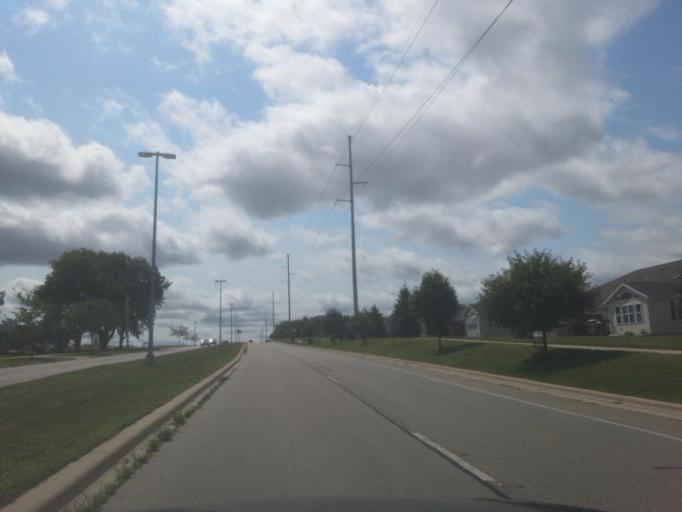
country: US
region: Wisconsin
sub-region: Dane County
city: Cottage Grove
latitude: 43.0911
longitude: -89.2671
